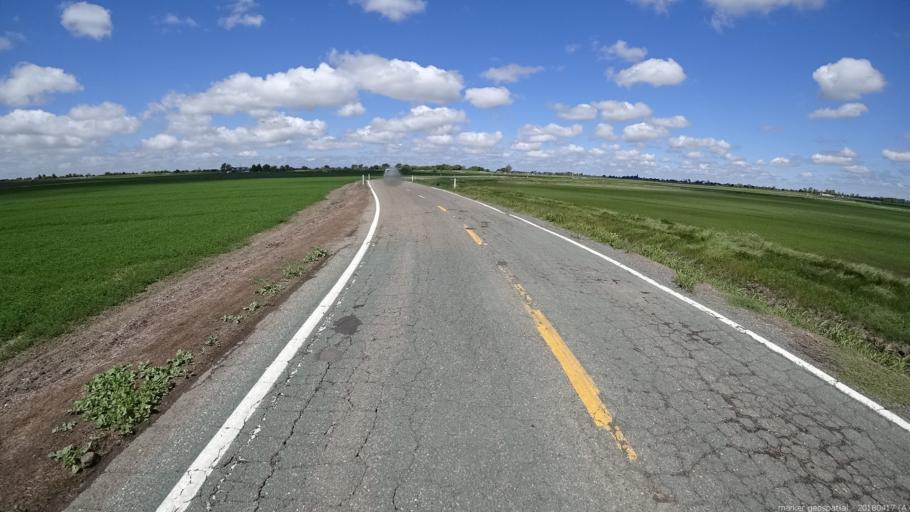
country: US
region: California
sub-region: Sacramento County
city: Walnut Grove
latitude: 38.2062
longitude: -121.5291
